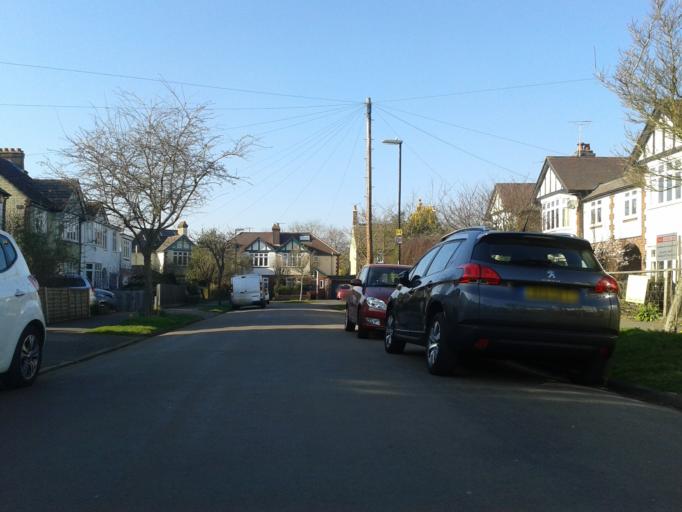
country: GB
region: England
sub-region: Cambridgeshire
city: Cambridge
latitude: 52.2216
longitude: 0.1264
